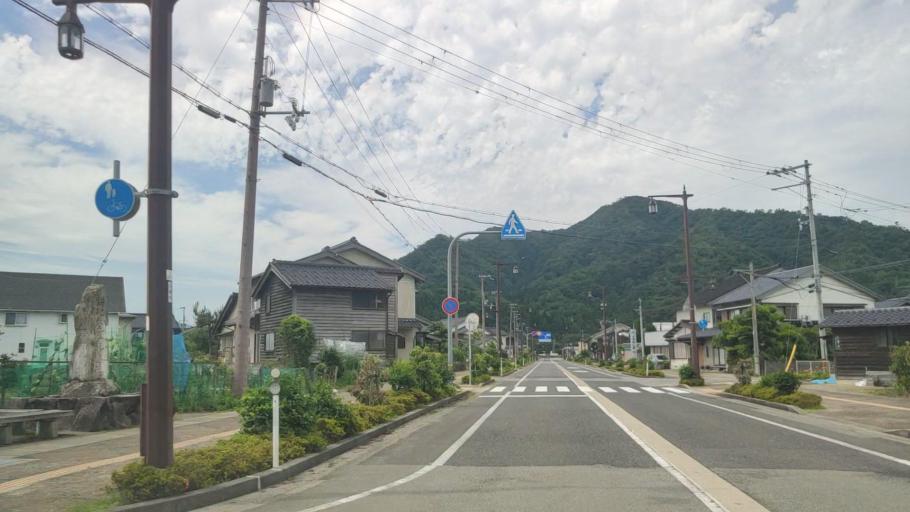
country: JP
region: Hyogo
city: Toyooka
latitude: 35.6524
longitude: 134.7591
